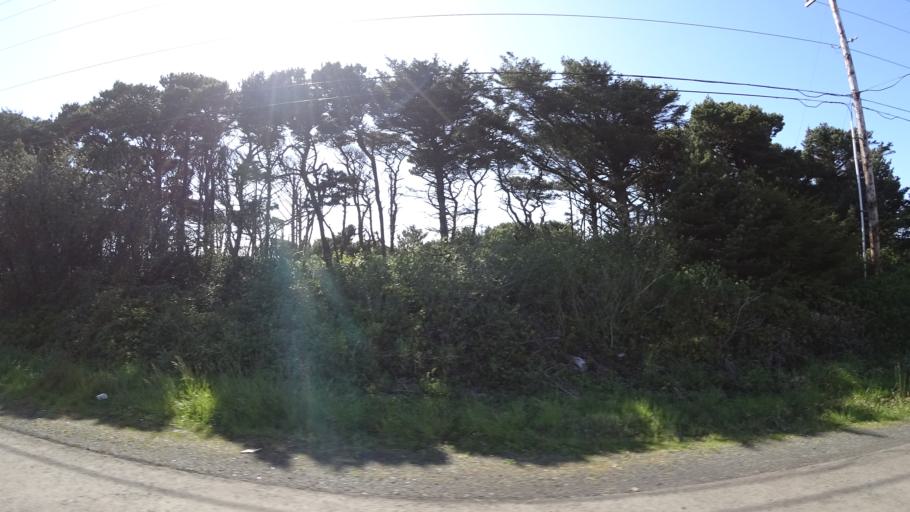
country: US
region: Oregon
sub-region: Lincoln County
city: Newport
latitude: 44.5534
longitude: -124.0720
